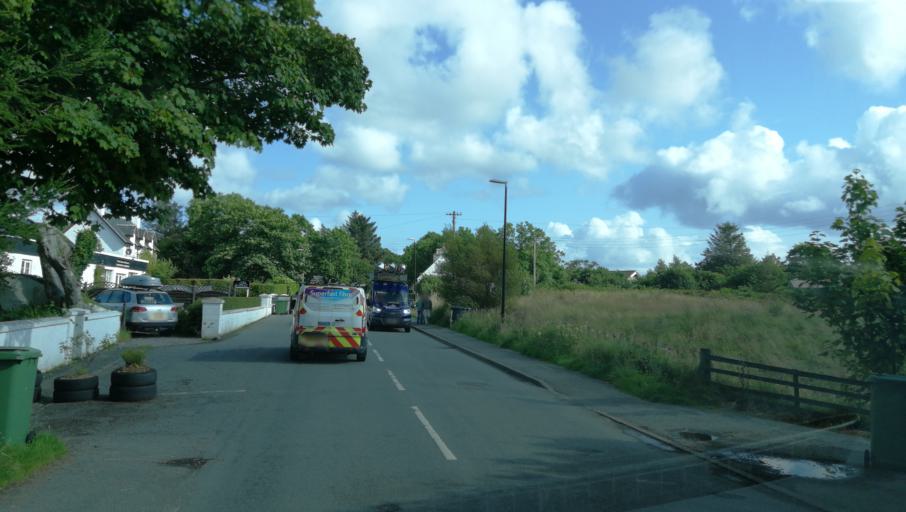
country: GB
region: Scotland
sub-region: Highland
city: Isle of Skye
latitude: 57.4323
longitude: -6.5738
